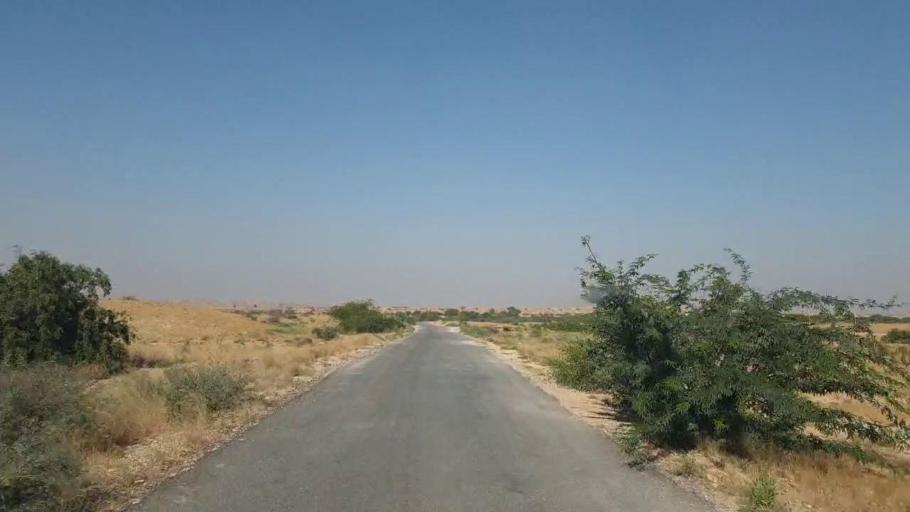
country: PK
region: Sindh
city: Thatta
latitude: 25.2098
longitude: 67.7975
